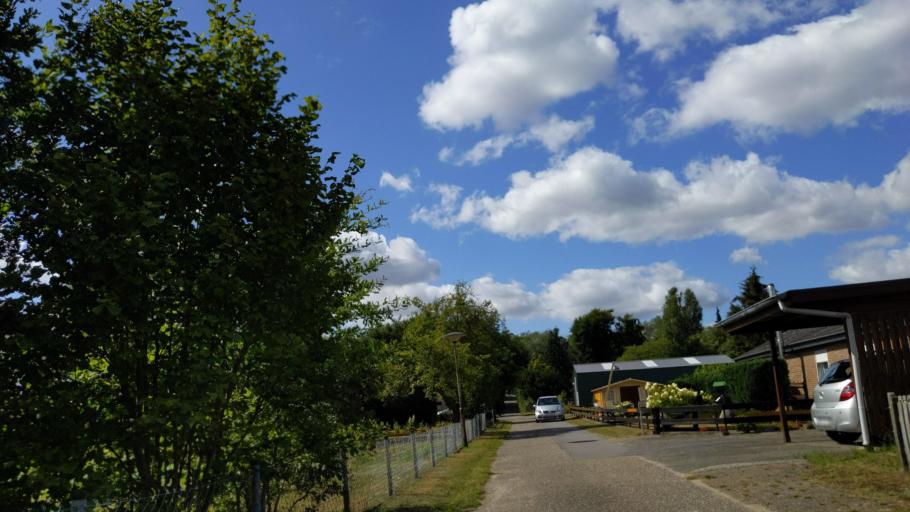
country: DE
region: Schleswig-Holstein
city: Ratekau
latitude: 53.8987
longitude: 10.7739
